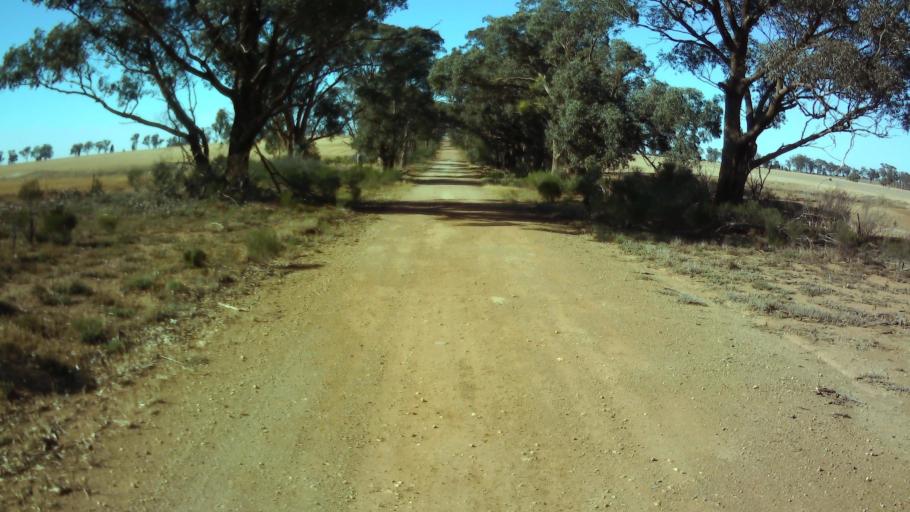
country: AU
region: New South Wales
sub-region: Weddin
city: Grenfell
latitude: -33.8926
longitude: 147.8802
